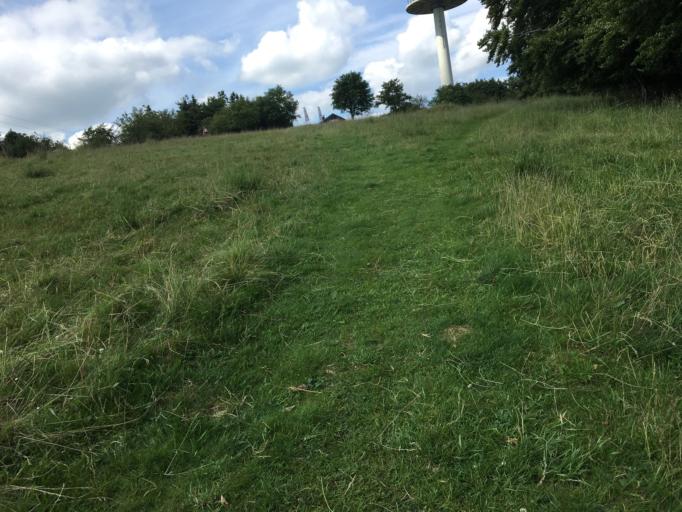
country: DE
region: Hesse
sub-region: Regierungsbezirk Giessen
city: Ulrichstein
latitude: 50.5080
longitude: 9.2259
